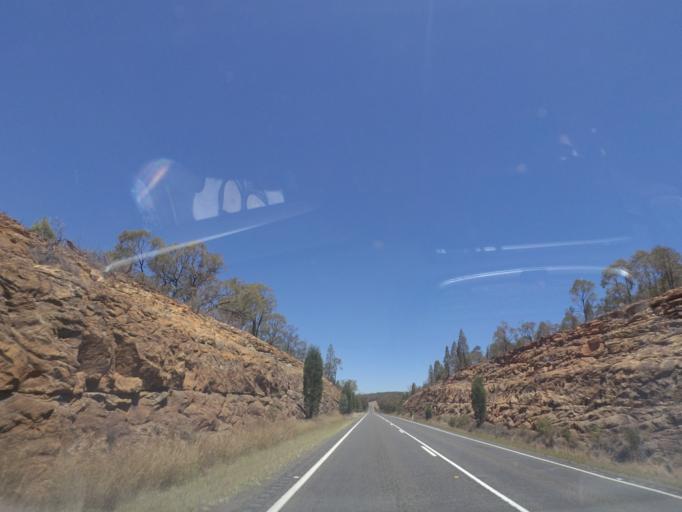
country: AU
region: New South Wales
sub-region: Warrumbungle Shire
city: Coonabarabran
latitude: -31.0688
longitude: 149.3922
